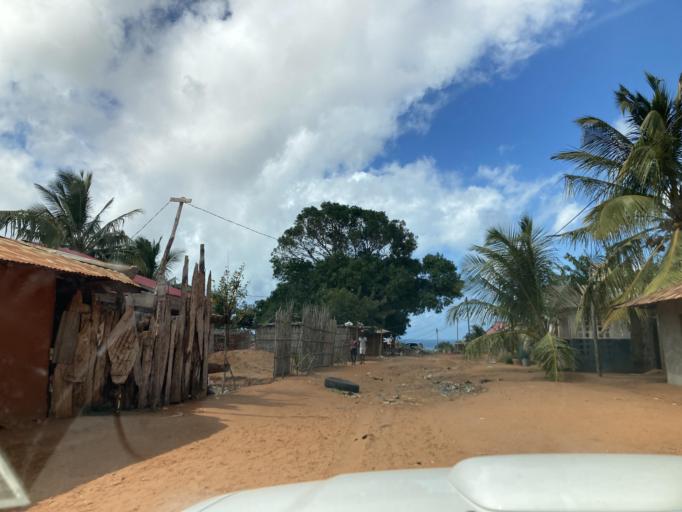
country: MZ
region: Cabo Delgado
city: Pemba
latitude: -13.0597
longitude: 40.5267
